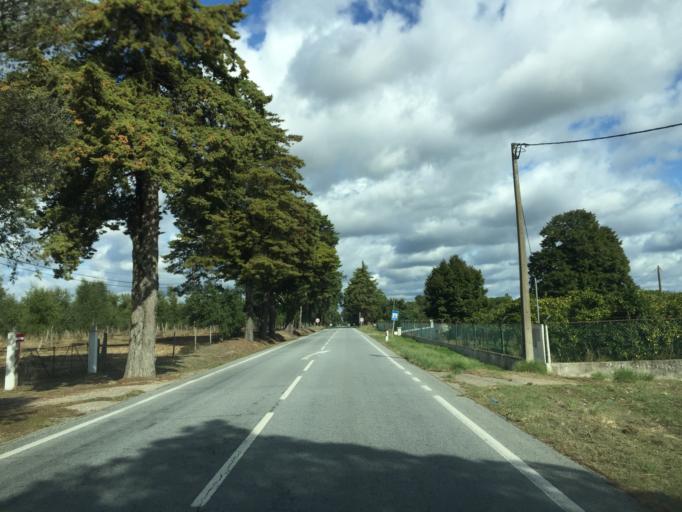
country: PT
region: Portalegre
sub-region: Ponte de Sor
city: Santo Andre
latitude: 39.0961
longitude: -8.1494
